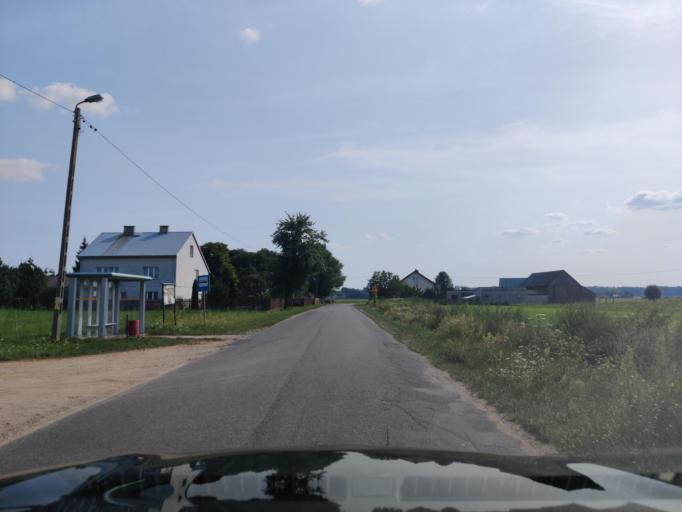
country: PL
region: Masovian Voivodeship
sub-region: Powiat wyszkowski
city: Rzasnik
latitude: 52.7448
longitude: 21.3533
